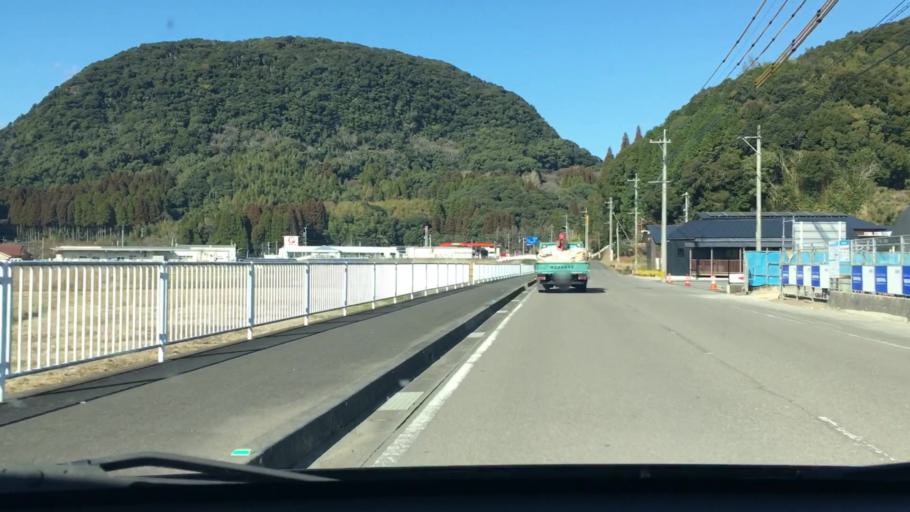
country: JP
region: Kagoshima
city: Satsumasendai
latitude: 31.7944
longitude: 130.4103
